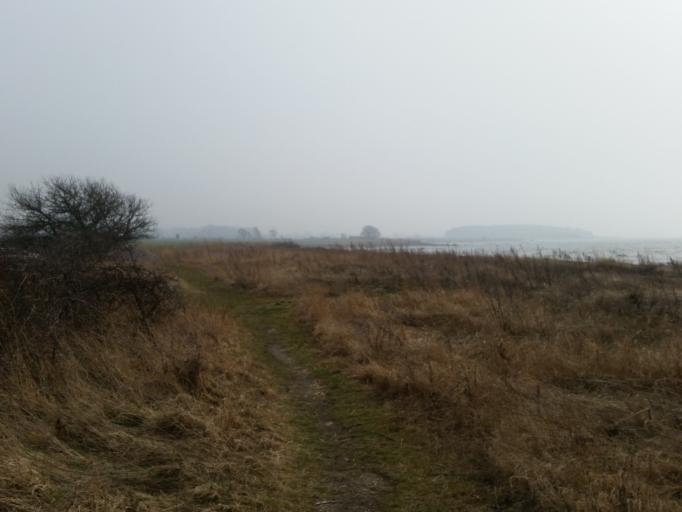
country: SE
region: Kalmar
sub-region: Morbylanga Kommun
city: Moerbylanga
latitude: 56.4155
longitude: 16.4051
